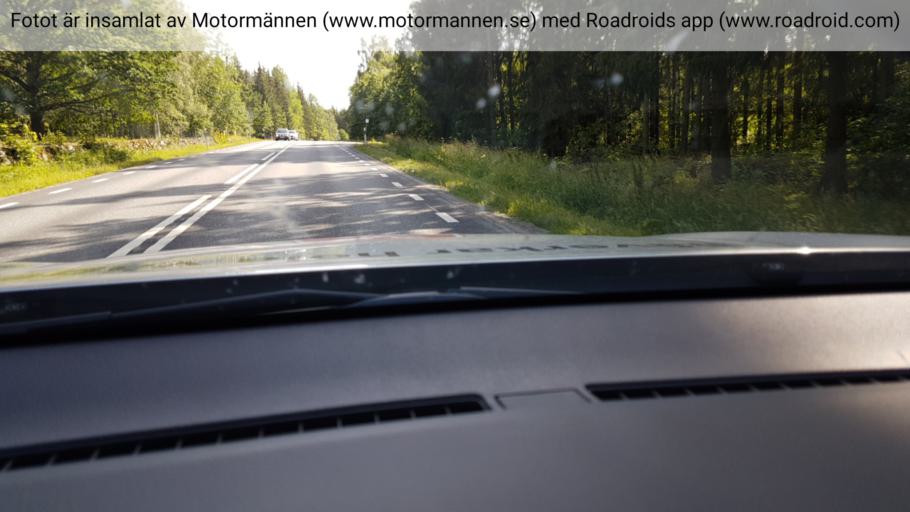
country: SE
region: Joenkoeping
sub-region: Aneby Kommun
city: Aneby
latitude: 57.8782
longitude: 14.8775
